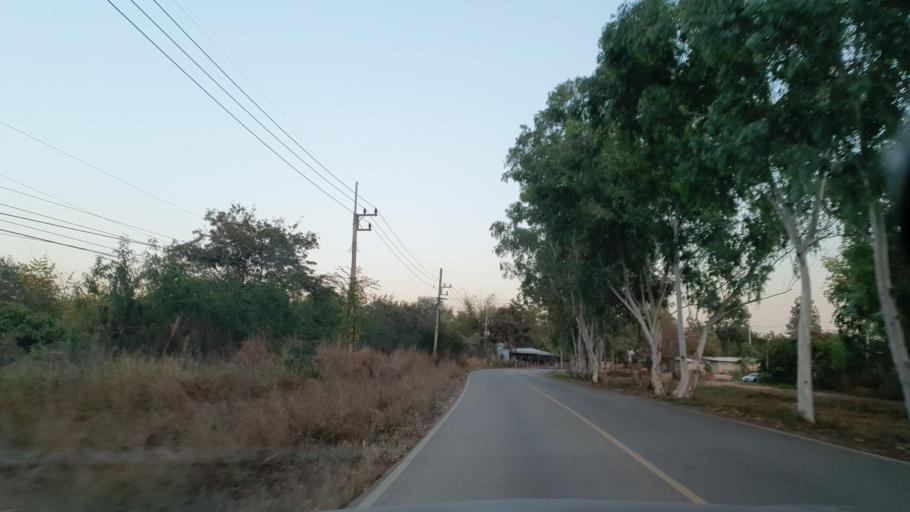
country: TH
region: Chiang Mai
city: Mae Wang
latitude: 18.6387
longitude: 98.7963
